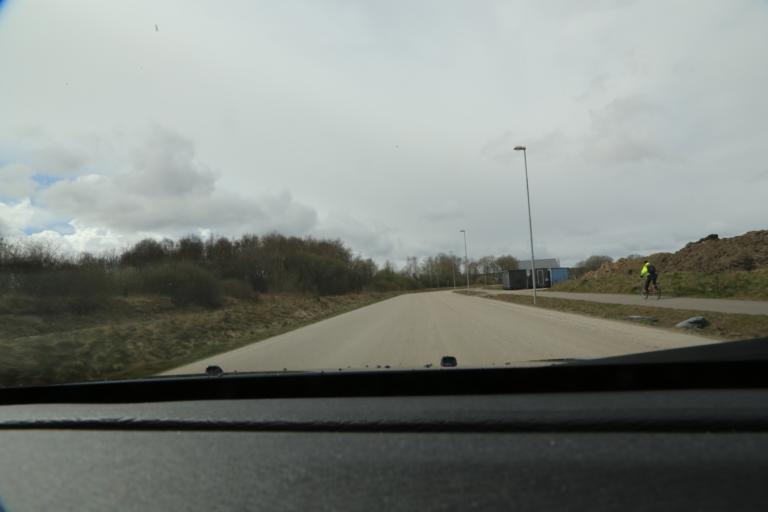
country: SE
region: Halland
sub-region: Varbergs Kommun
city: Varberg
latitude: 57.1185
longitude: 12.3003
